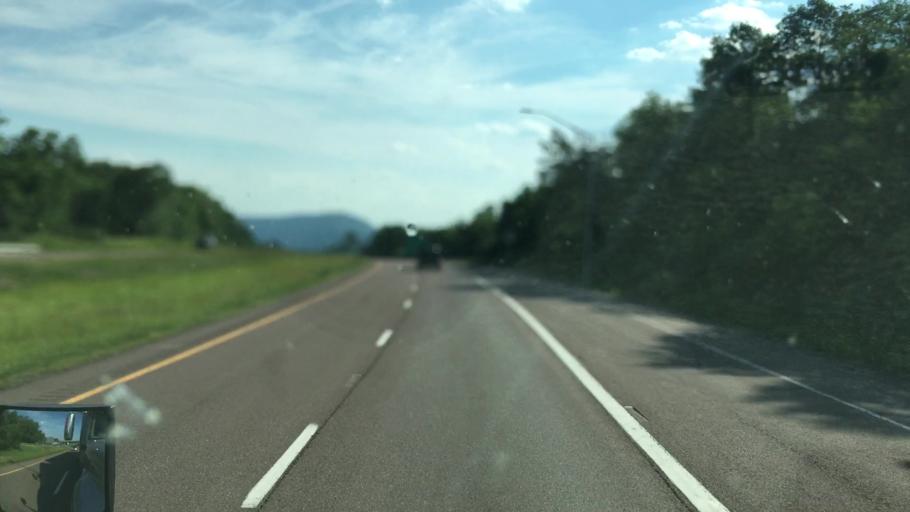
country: US
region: Maryland
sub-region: Allegany County
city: Cumberland
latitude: 39.6651
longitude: -78.7397
